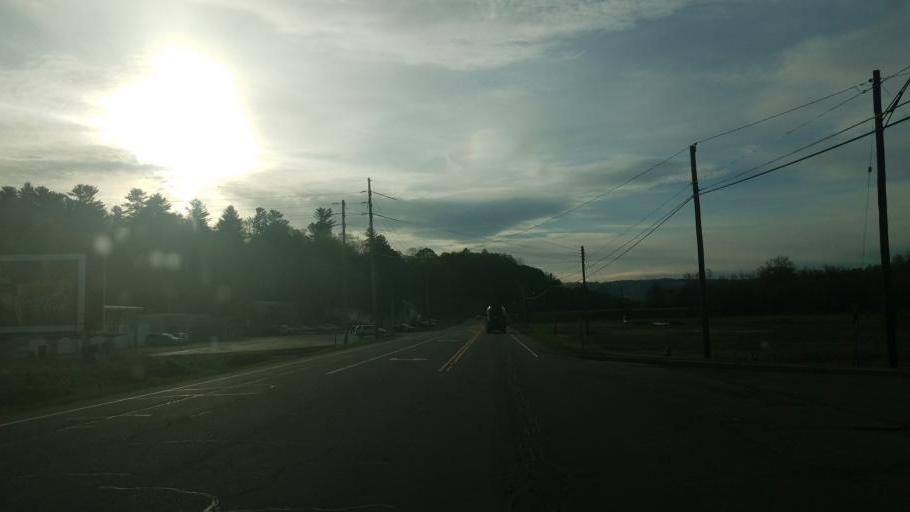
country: US
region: New York
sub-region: Steuben County
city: Hornell
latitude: 42.3342
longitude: -77.6786
